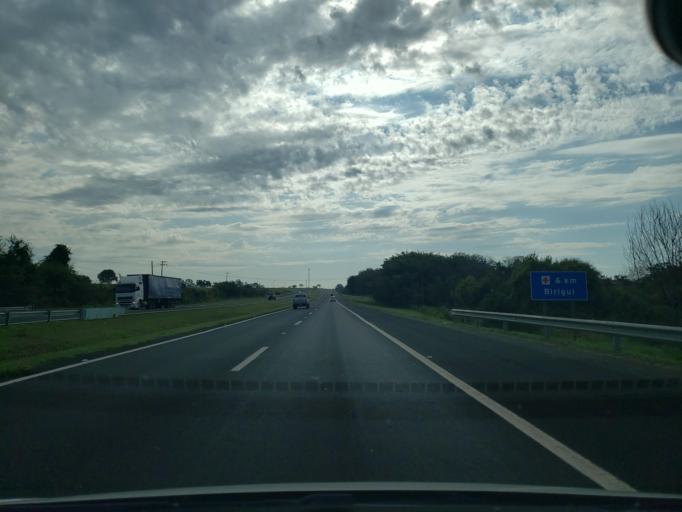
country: BR
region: Sao Paulo
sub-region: Birigui
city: Birigui
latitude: -21.3489
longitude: -50.3144
